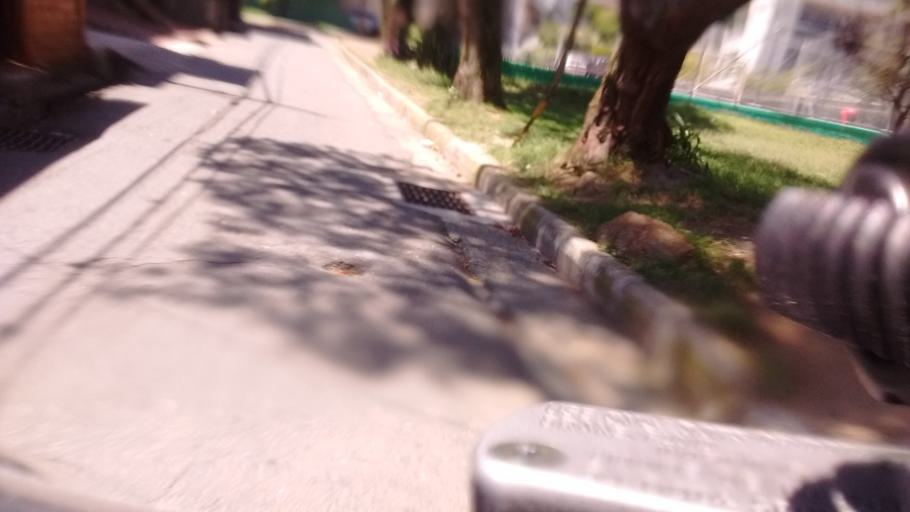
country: CO
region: Antioquia
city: Medellin
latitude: 6.2847
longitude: -75.5827
